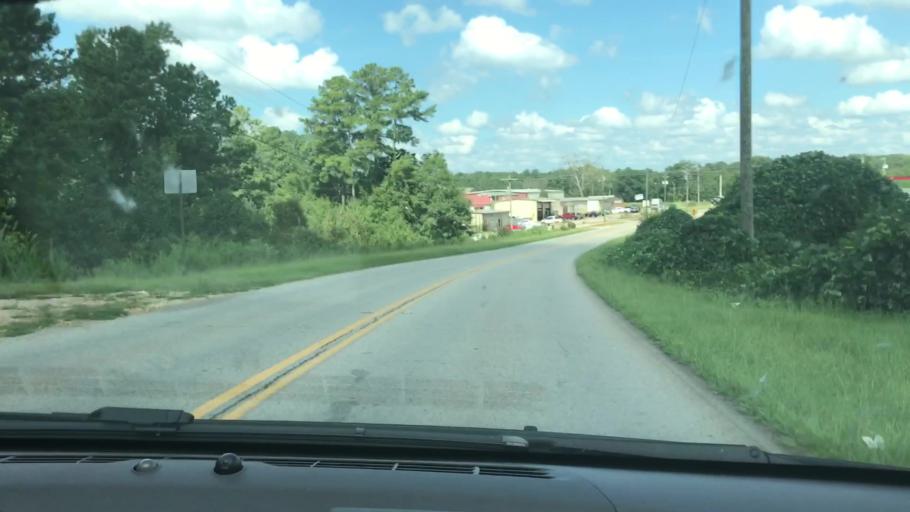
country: US
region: Georgia
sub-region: Troup County
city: La Grange
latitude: 33.0193
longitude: -85.0794
